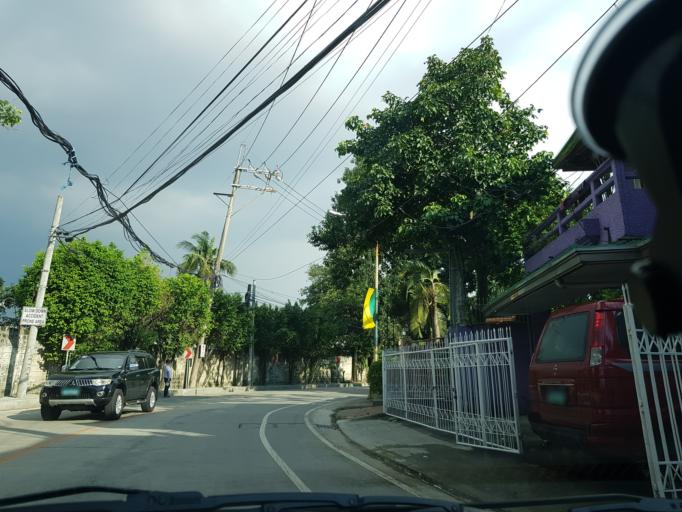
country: PH
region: Metro Manila
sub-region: Marikina
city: Calumpang
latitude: 14.6173
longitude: 121.0861
